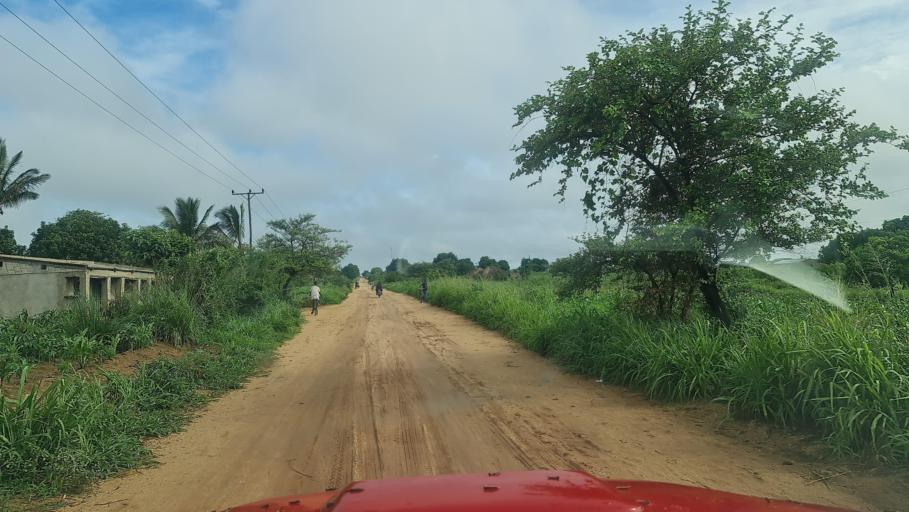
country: MW
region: Southern Region
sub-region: Nsanje District
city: Nsanje
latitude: -17.3097
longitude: 35.5928
